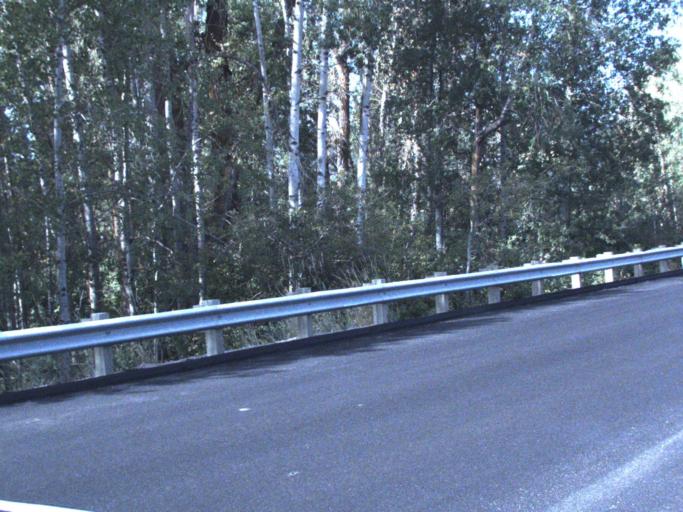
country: US
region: Washington
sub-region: Stevens County
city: Colville
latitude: 48.4796
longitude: -117.8992
